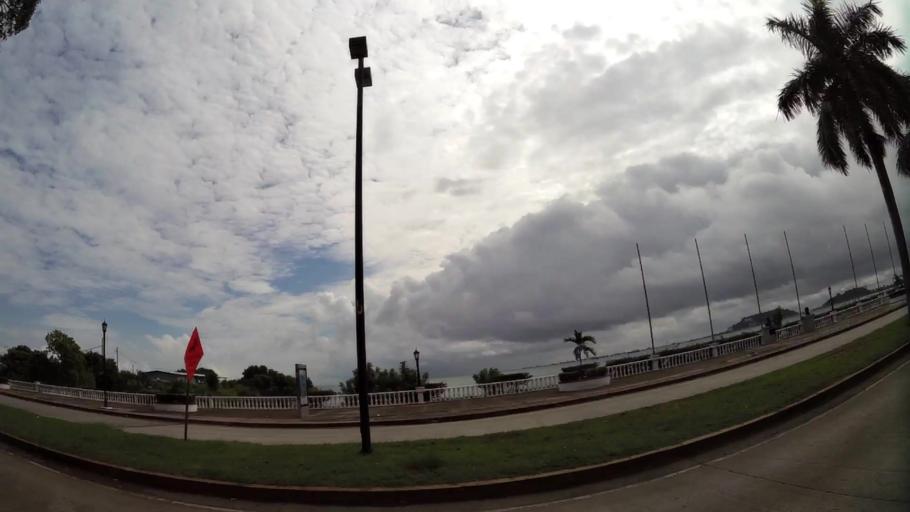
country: PA
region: Panama
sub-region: Distrito de Panama
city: Ancon
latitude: 8.9356
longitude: -79.5453
